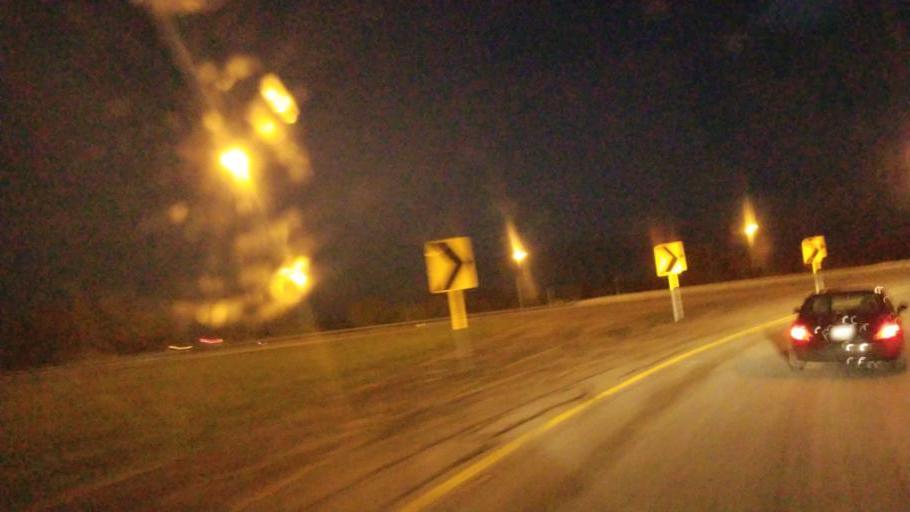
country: US
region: Ohio
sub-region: Richland County
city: Lincoln Heights
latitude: 40.7838
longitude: -82.4124
